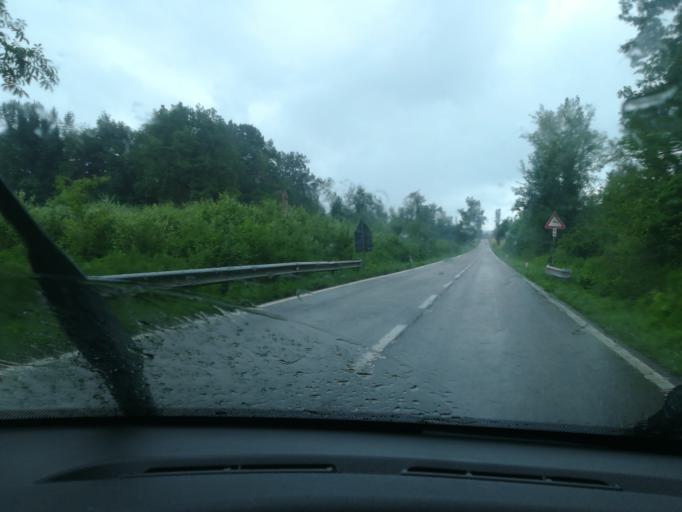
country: IT
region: The Marches
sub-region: Provincia di Macerata
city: Sarnano
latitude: 43.0294
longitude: 13.3143
